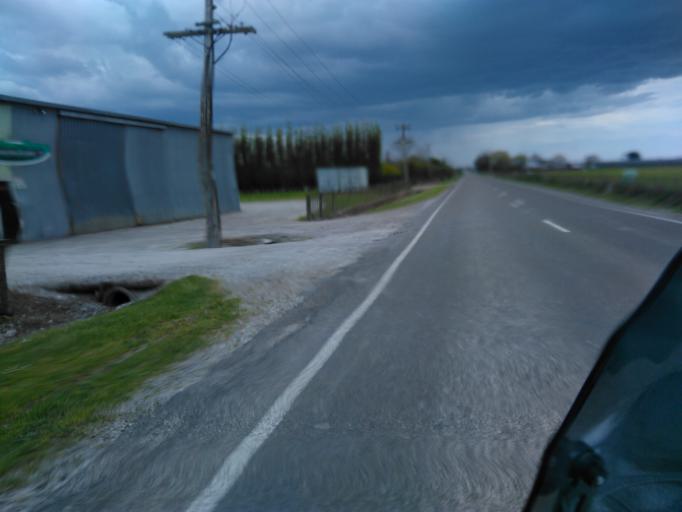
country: NZ
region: Gisborne
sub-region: Gisborne District
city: Gisborne
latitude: -38.6459
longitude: 177.9044
